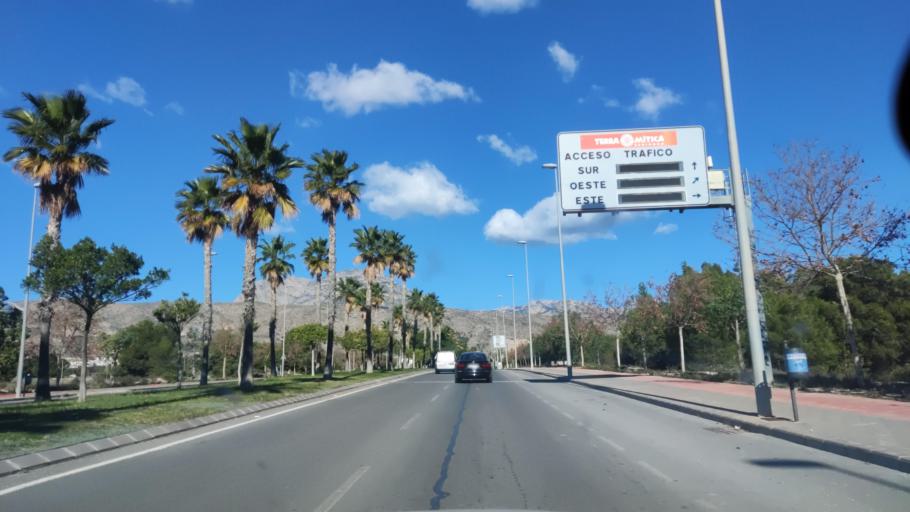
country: ES
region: Valencia
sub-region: Provincia de Alicante
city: Benidorm
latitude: 38.5403
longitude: -0.1592
